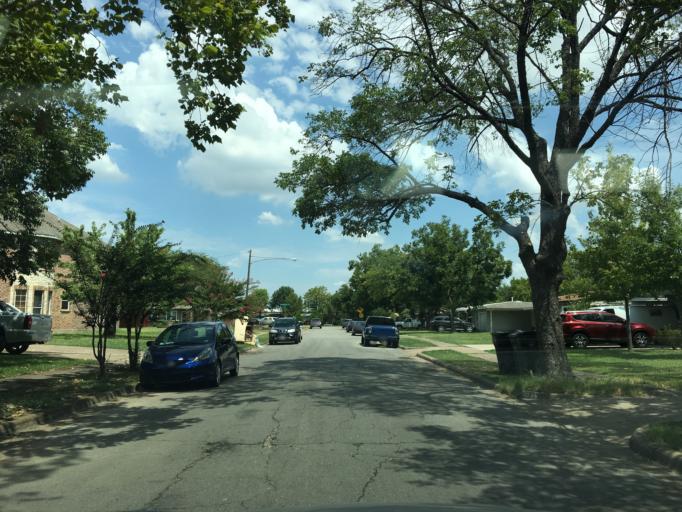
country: US
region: Texas
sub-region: Dallas County
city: Garland
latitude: 32.8611
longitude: -96.6749
